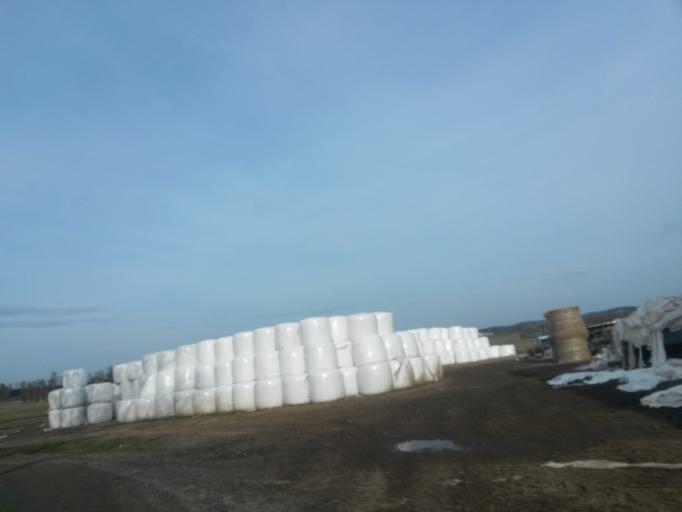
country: SE
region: Vaestra Goetaland
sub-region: Vargarda Kommun
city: Jonstorp
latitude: 58.0122
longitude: 12.7399
